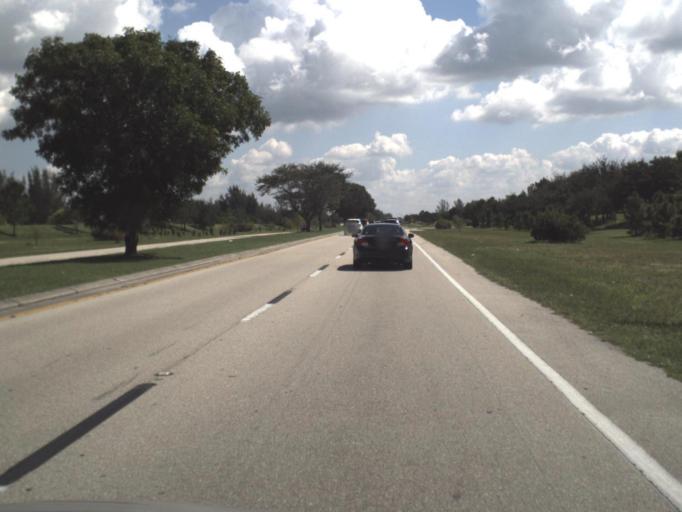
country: US
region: Florida
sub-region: Lee County
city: Cape Coral
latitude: 26.6069
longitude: -82.0036
